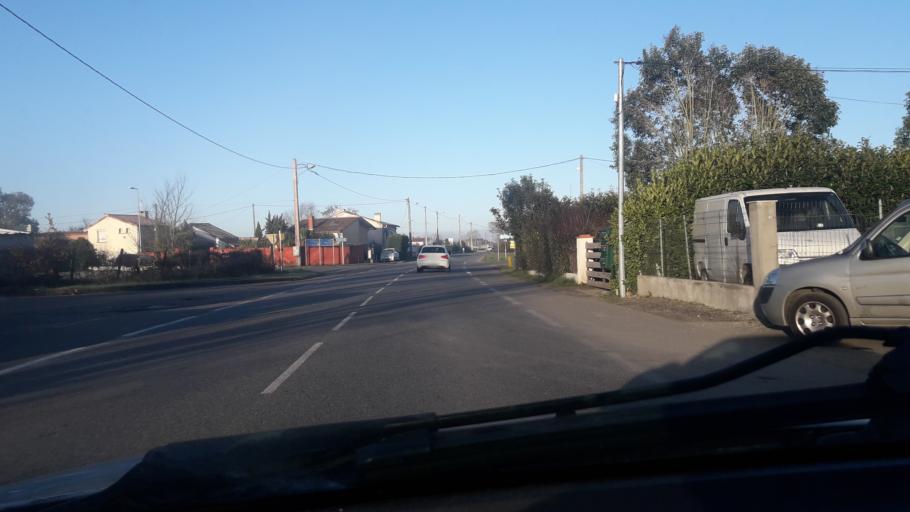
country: FR
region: Midi-Pyrenees
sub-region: Departement de la Haute-Garonne
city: Carbonne
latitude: 43.2963
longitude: 1.2070
